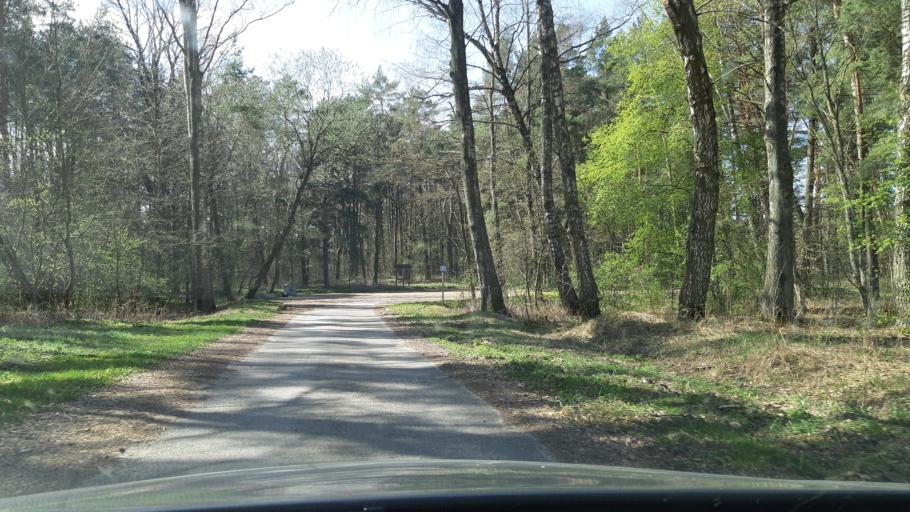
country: LT
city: Virbalis
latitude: 54.5694
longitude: 22.9061
